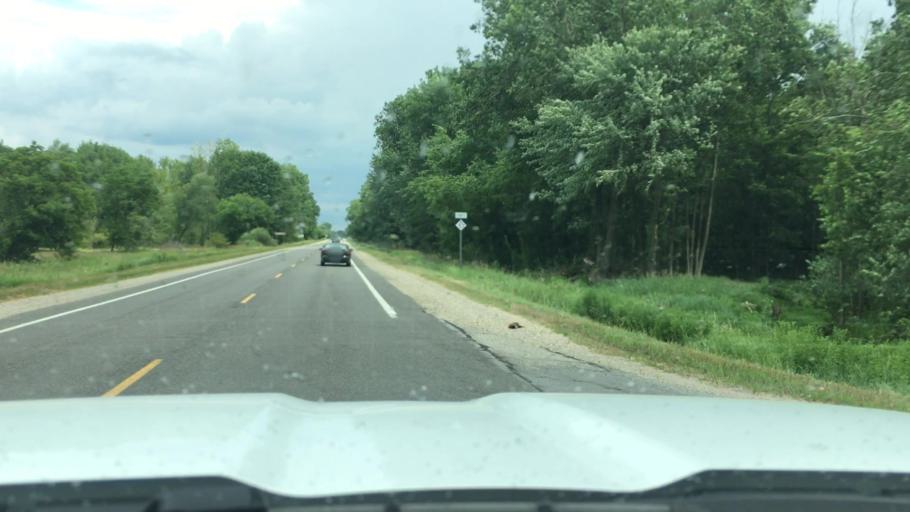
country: US
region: Michigan
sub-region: Montcalm County
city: Stanton
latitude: 43.1776
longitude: -85.0146
